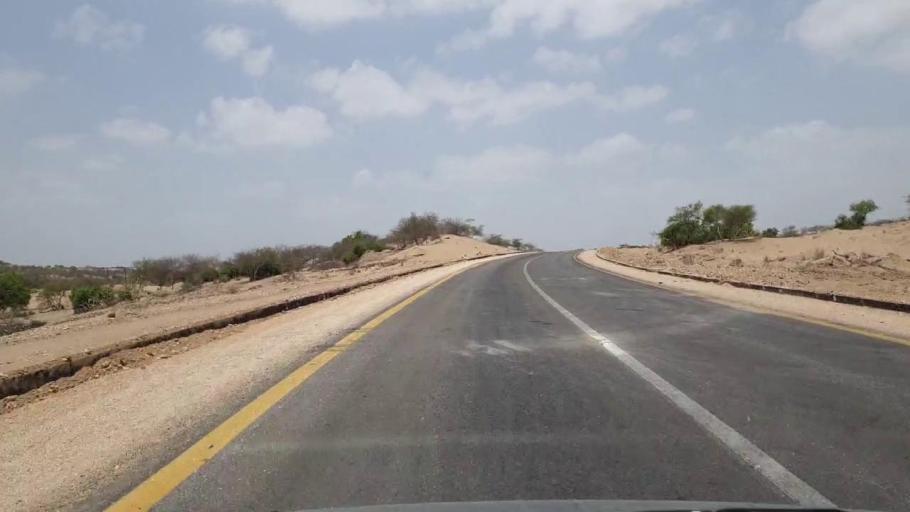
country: PK
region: Sindh
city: Mithi
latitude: 24.8360
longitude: 69.6360
